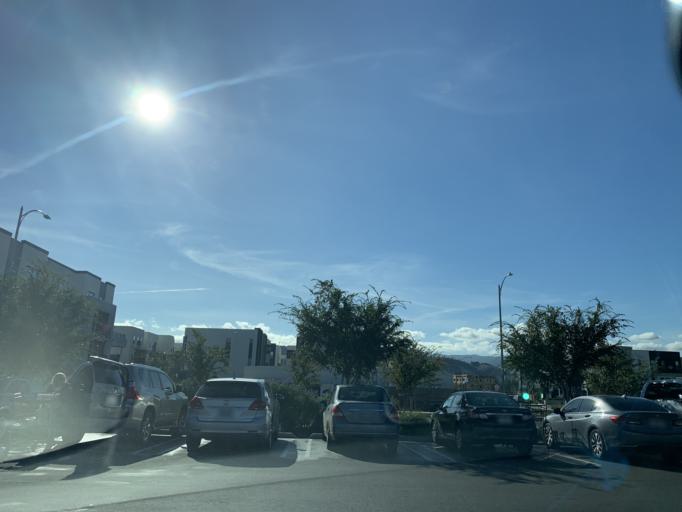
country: US
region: California
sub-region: Santa Clara County
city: Seven Trees
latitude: 37.2432
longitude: -121.7864
